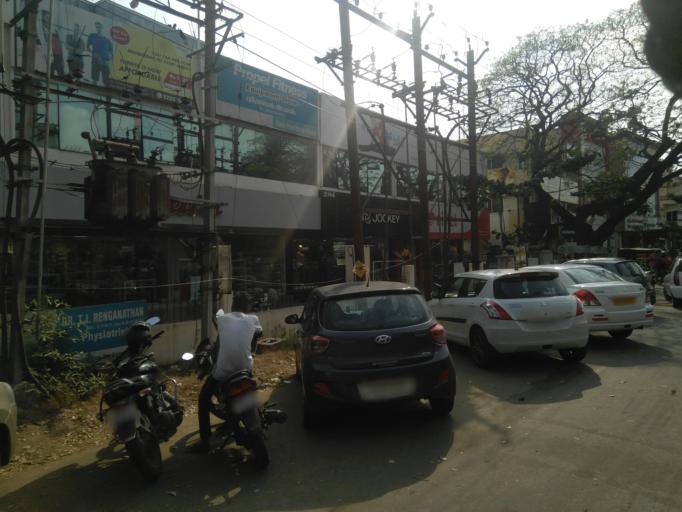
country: IN
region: Tamil Nadu
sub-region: Coimbatore
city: Coimbatore
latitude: 10.9977
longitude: 76.9868
